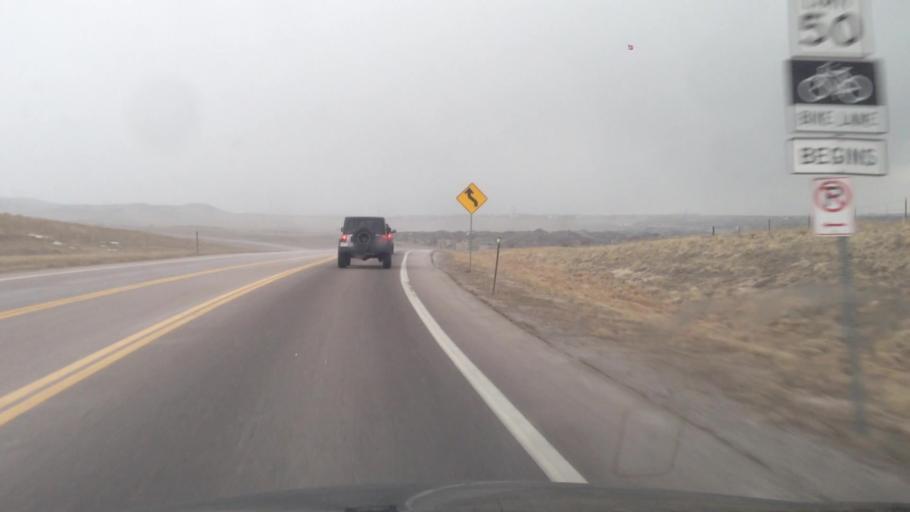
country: US
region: Colorado
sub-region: Douglas County
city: Stonegate
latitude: 39.4933
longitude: -104.8134
